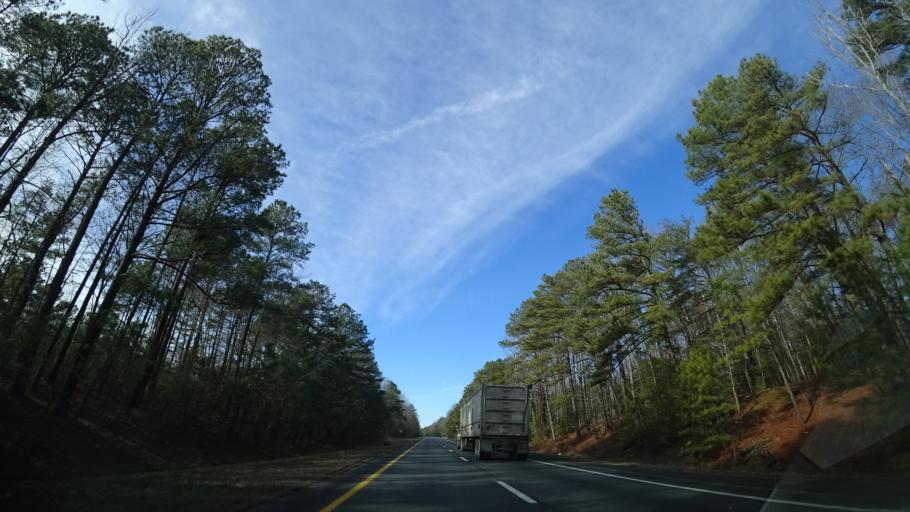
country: US
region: Virginia
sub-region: New Kent County
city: New Kent
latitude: 37.5055
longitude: -77.0968
